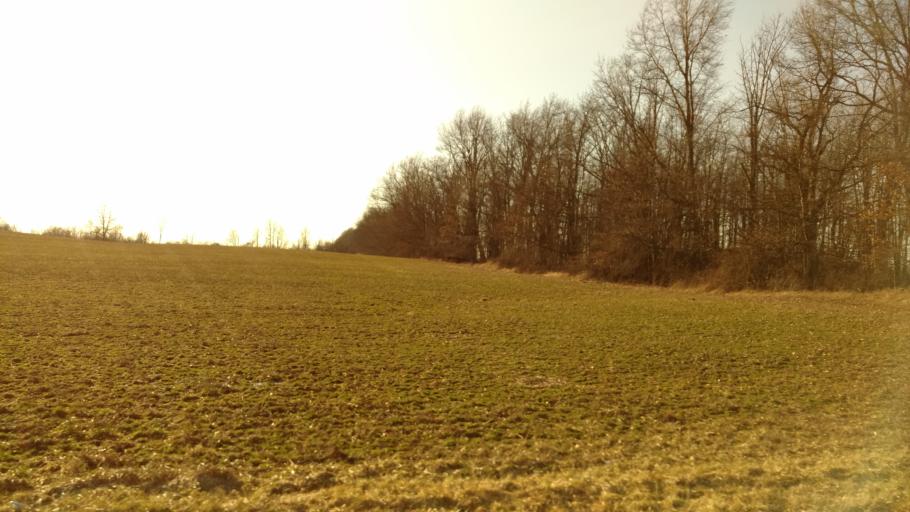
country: US
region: Ohio
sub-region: Richland County
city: Ontario
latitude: 40.7391
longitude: -82.6082
